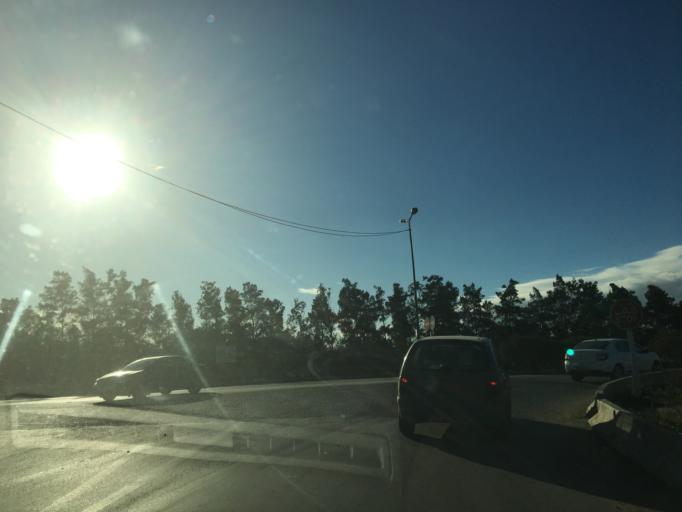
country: DZ
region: Tipaza
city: Baraki
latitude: 36.6863
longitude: 3.1151
